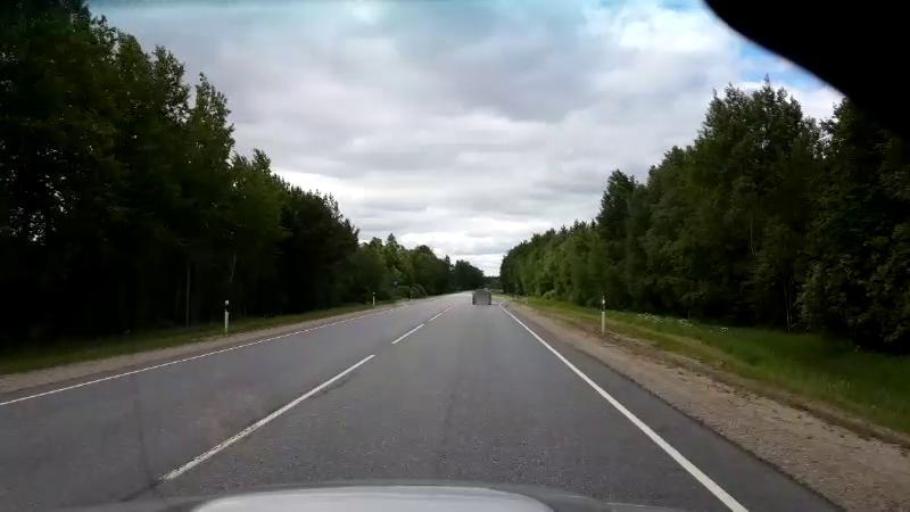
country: EE
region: Raplamaa
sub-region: Maerjamaa vald
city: Marjamaa
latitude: 58.9470
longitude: 24.4676
